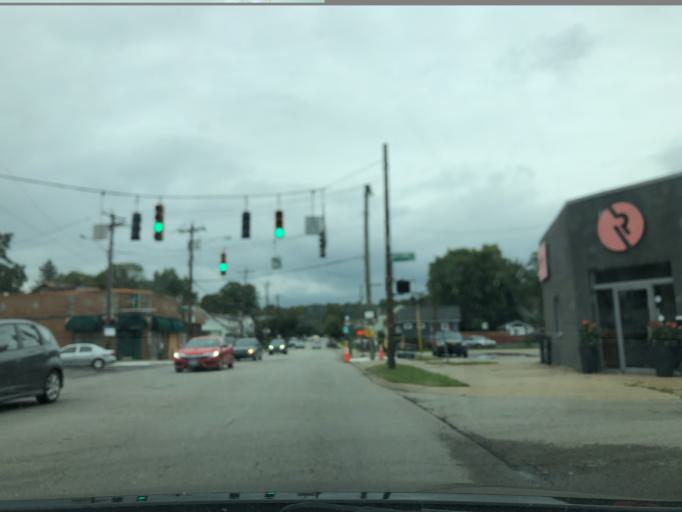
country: US
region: Ohio
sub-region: Hamilton County
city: Mariemont
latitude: 39.1504
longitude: -84.3796
